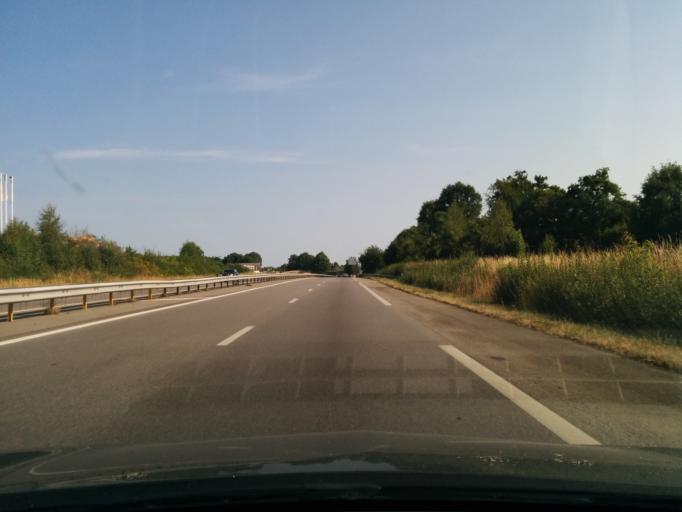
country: FR
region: Limousin
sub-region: Departement de la Haute-Vienne
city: Boisseuil
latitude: 45.7610
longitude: 1.3304
